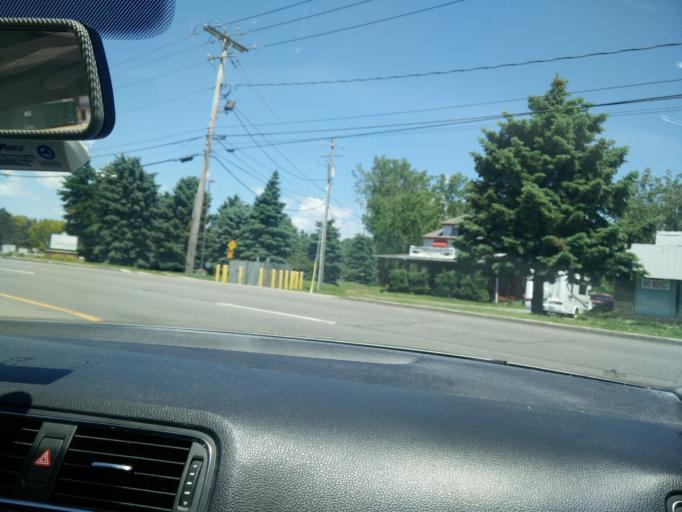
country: US
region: New York
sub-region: Erie County
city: West Seneca
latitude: 42.8312
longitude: -78.7776
